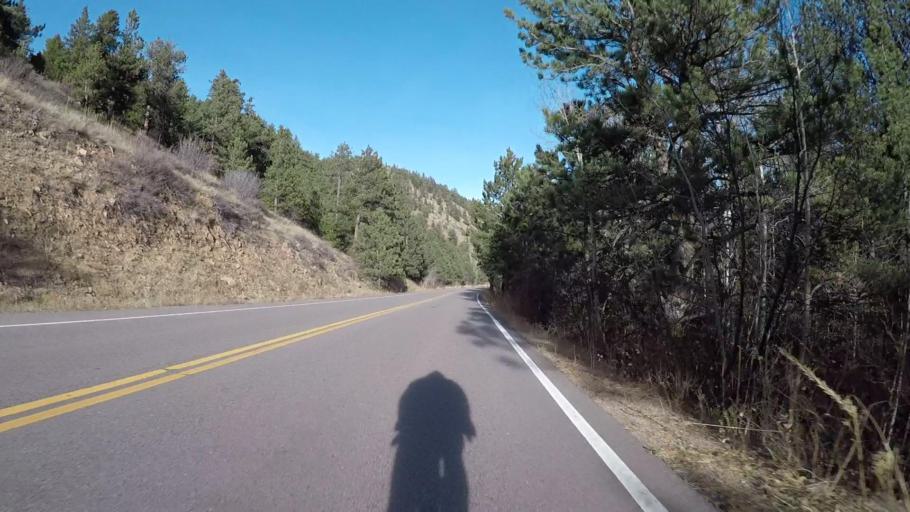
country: US
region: Colorado
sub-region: Boulder County
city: Nederland
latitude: 40.0653
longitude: -105.4590
